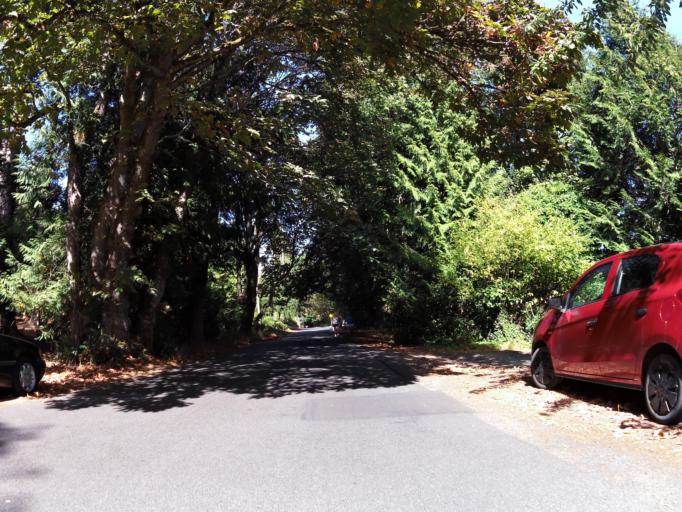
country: CA
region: British Columbia
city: Victoria
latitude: 48.5122
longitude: -123.3665
